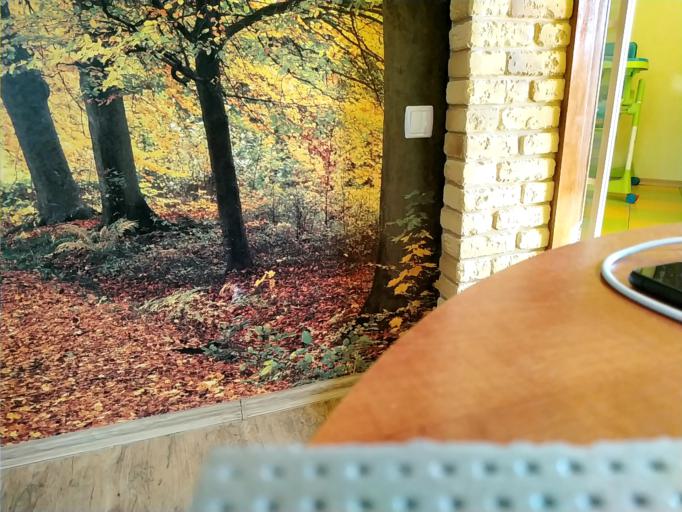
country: RU
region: Tverskaya
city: Kalashnikovo
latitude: 57.3488
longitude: 35.1980
